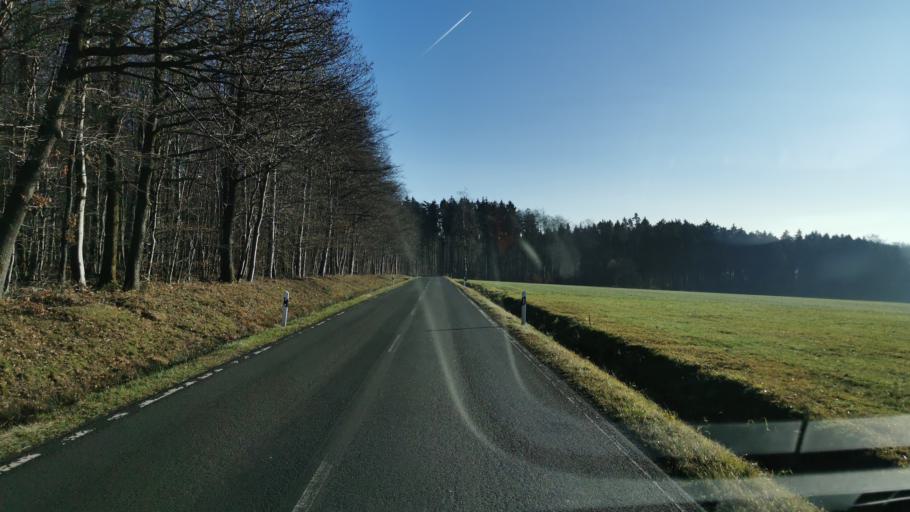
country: DE
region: Rheinland-Pfalz
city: Meisburg
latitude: 50.1144
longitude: 6.6933
